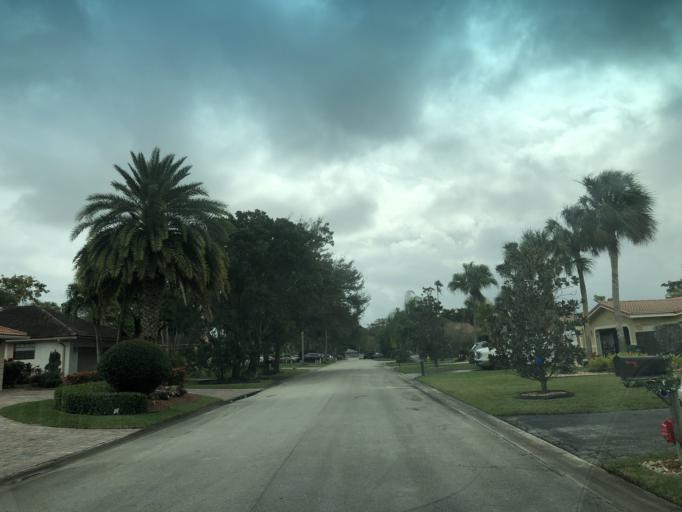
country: US
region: Florida
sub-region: Broward County
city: Margate
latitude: 26.2516
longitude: -80.2348
